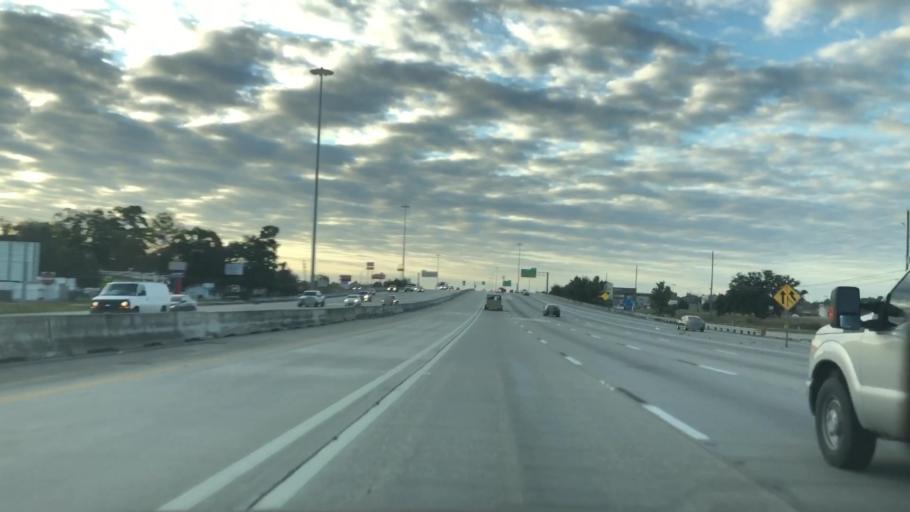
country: US
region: Texas
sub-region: Harris County
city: Spring
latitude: 30.0793
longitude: -95.4370
